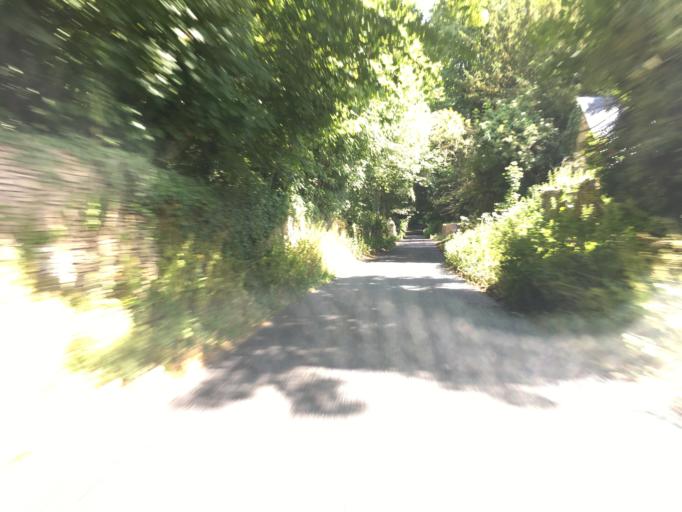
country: GB
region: England
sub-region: Gloucestershire
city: Tetbury
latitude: 51.6561
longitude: -2.1858
